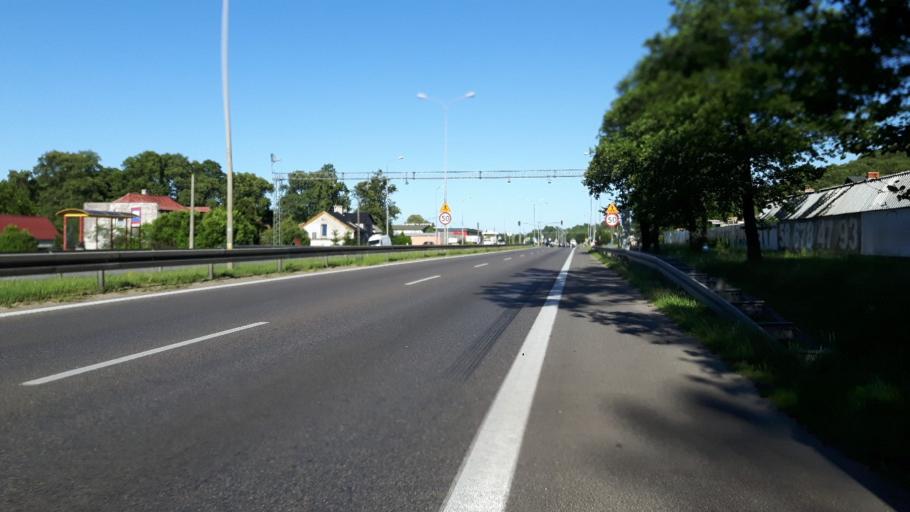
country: PL
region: Pomeranian Voivodeship
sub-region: Powiat wejherowski
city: Reda
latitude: 54.6048
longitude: 18.3150
